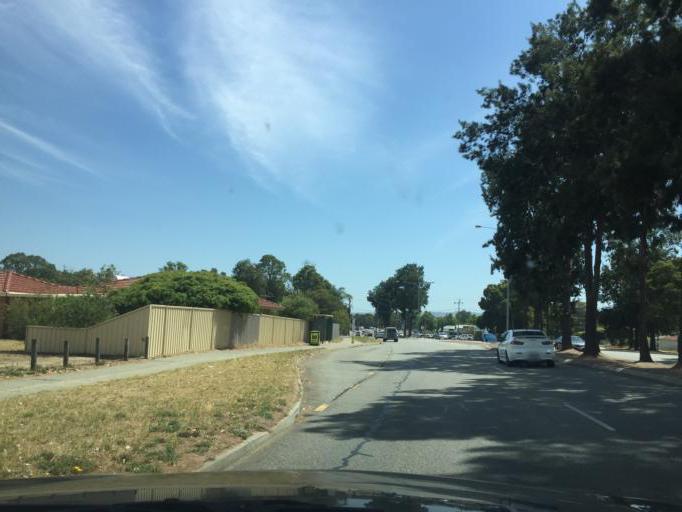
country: AU
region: Western Australia
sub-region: Gosnells
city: Thornlie
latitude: -32.0693
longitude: 115.9686
